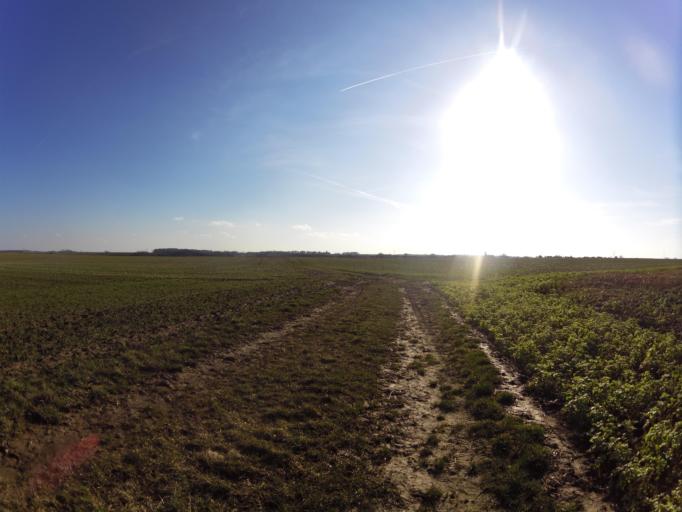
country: DE
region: Bavaria
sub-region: Regierungsbezirk Unterfranken
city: Giebelstadt
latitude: 49.6785
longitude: 9.9677
